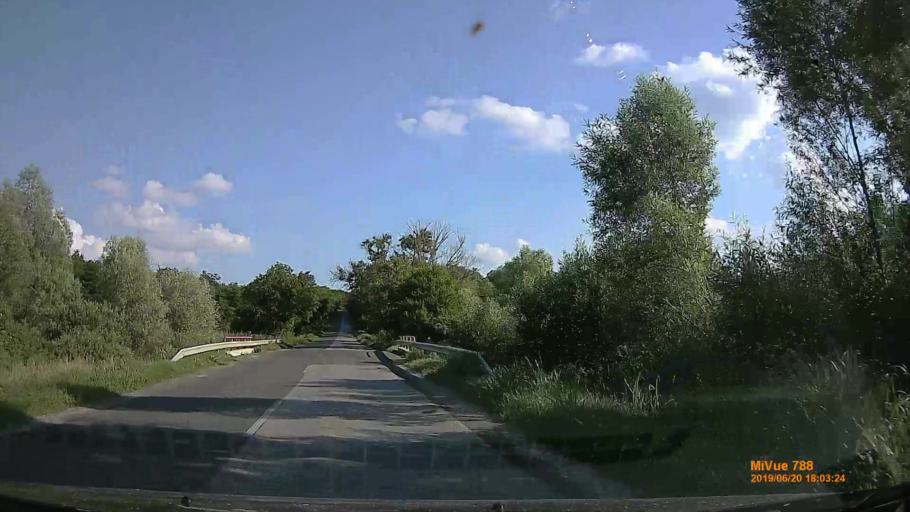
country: HU
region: Baranya
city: Szentlorinc
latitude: 46.0620
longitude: 17.9908
